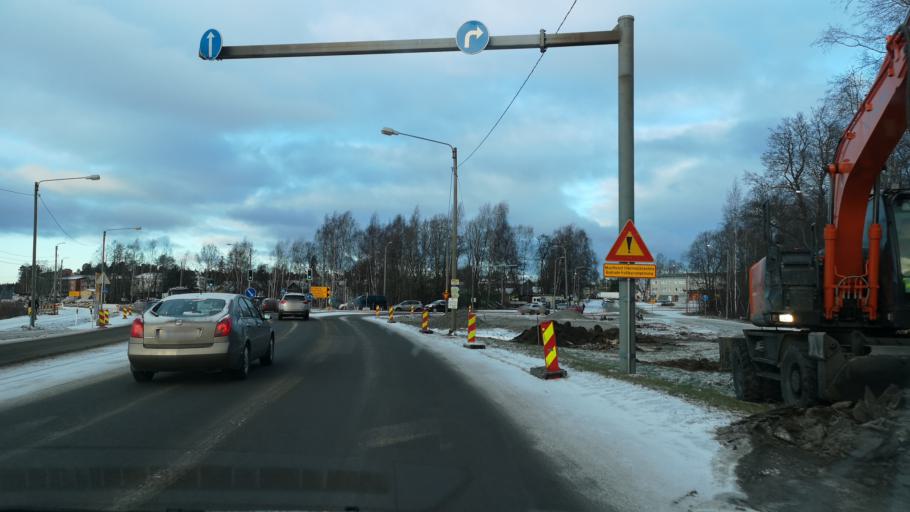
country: FI
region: Ostrobothnia
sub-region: Vaasa
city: Vaasa
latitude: 63.1130
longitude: 21.6185
